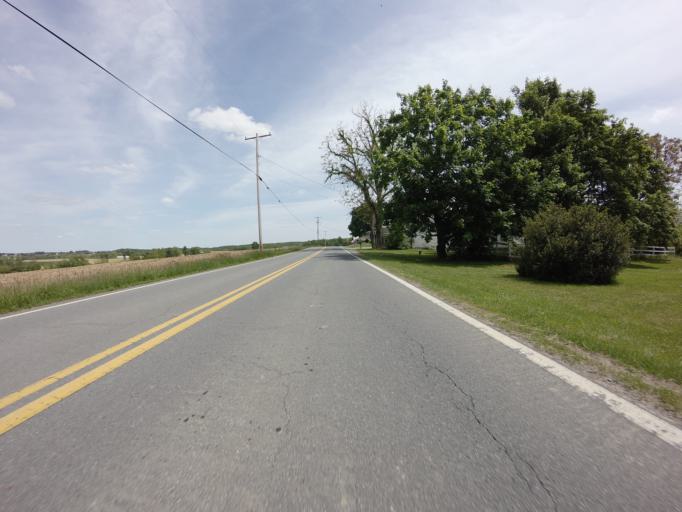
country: US
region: Maryland
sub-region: Frederick County
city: Woodsboro
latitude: 39.5291
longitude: -77.2826
